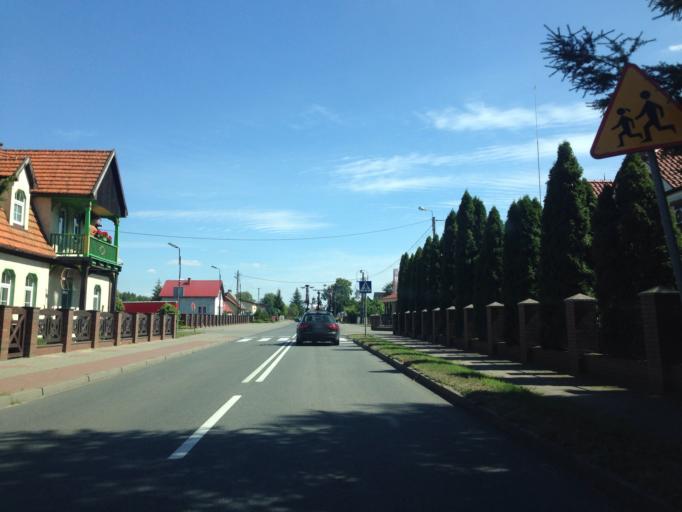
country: PL
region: Kujawsko-Pomorskie
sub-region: Powiat swiecki
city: Osie
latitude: 53.6040
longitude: 18.3331
